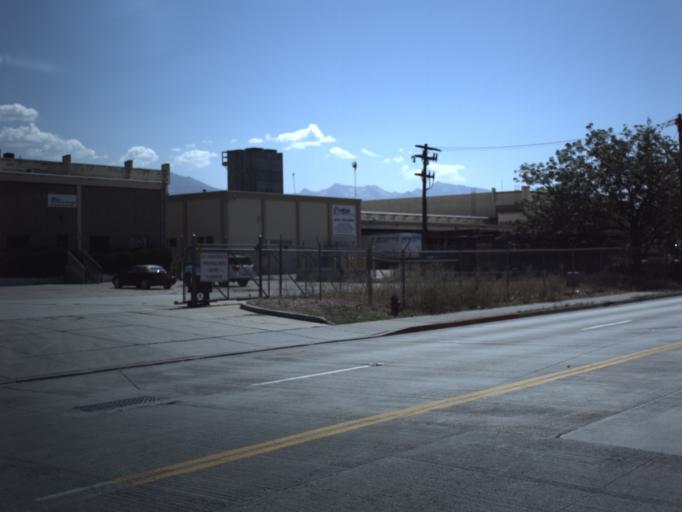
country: US
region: Utah
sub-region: Salt Lake County
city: South Salt Lake
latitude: 40.7222
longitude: -111.9175
